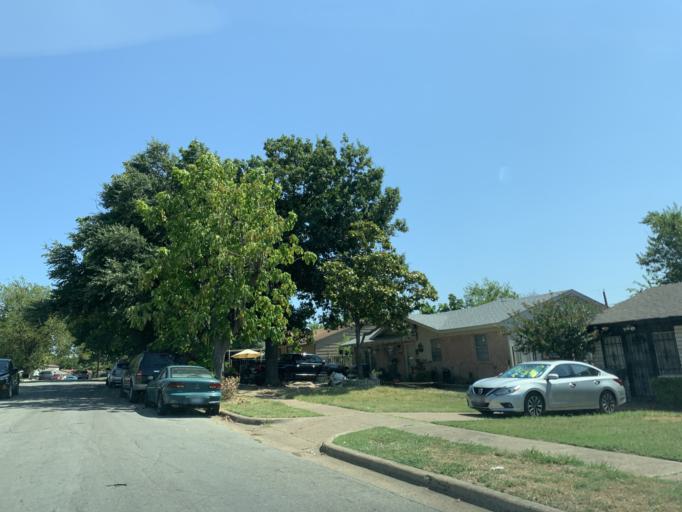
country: US
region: Texas
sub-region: Dallas County
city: Hutchins
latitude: 32.6707
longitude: -96.7574
